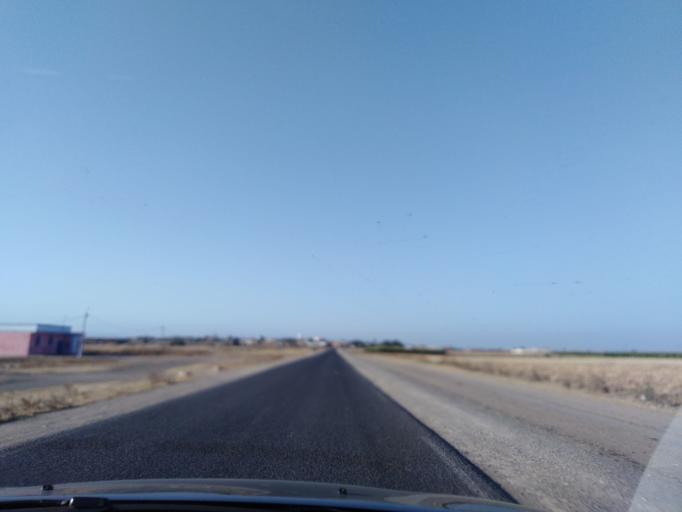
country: MA
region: Doukkala-Abda
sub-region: Safi
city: Safi
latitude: 32.5220
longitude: -8.9089
